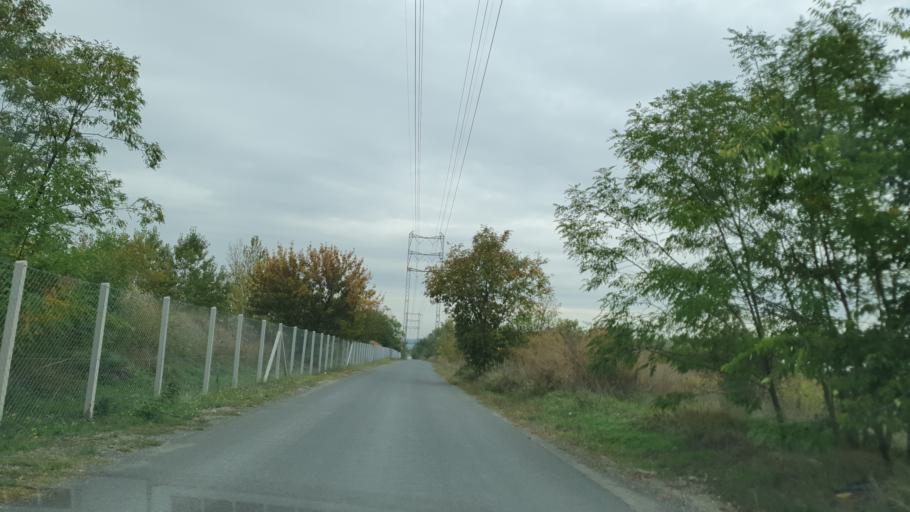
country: HU
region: Budapest
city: Budapest XXI. keruelet
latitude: 47.3941
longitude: 19.0674
